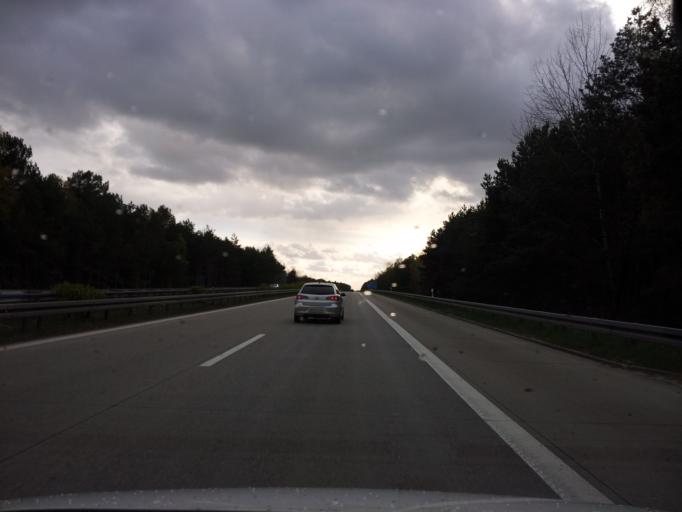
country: DE
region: Brandenburg
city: Heinersbruck
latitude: 51.7108
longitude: 14.4548
